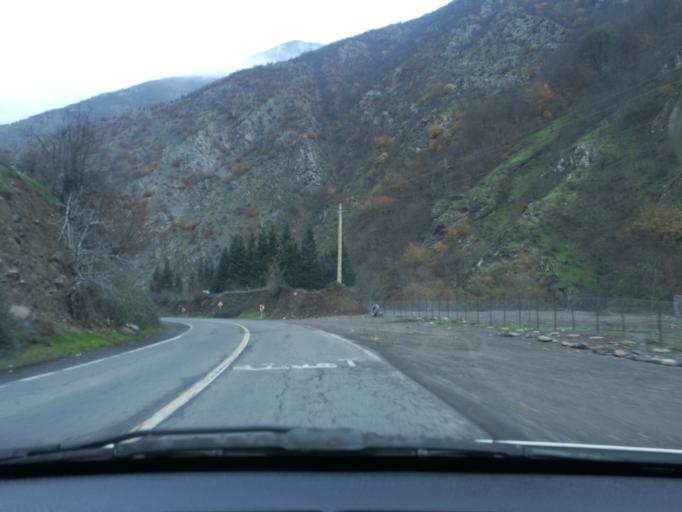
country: IR
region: Mazandaran
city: Chalus
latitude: 36.3473
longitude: 51.2593
